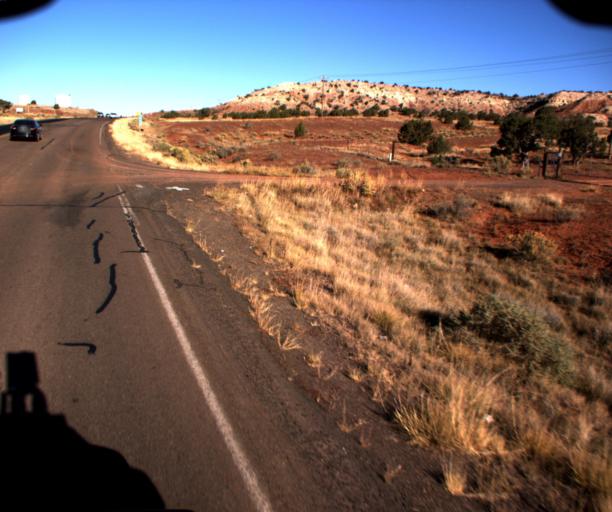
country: US
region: Arizona
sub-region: Apache County
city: Ganado
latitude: 35.7338
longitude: -109.6022
